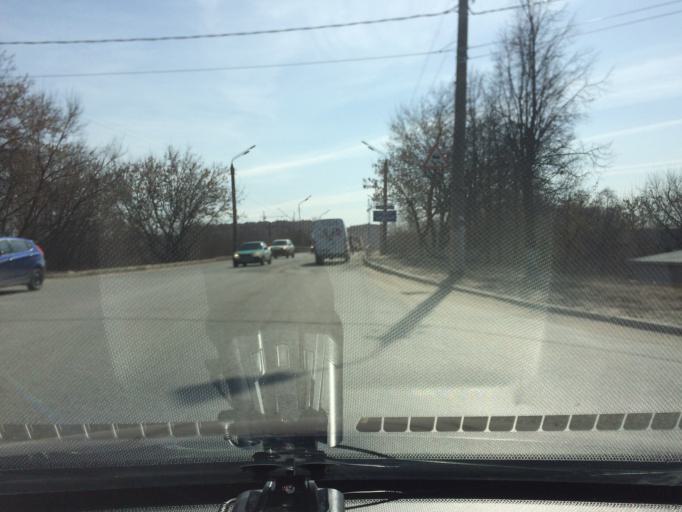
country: RU
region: Mariy-El
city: Yoshkar-Ola
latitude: 56.6452
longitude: 47.9094
